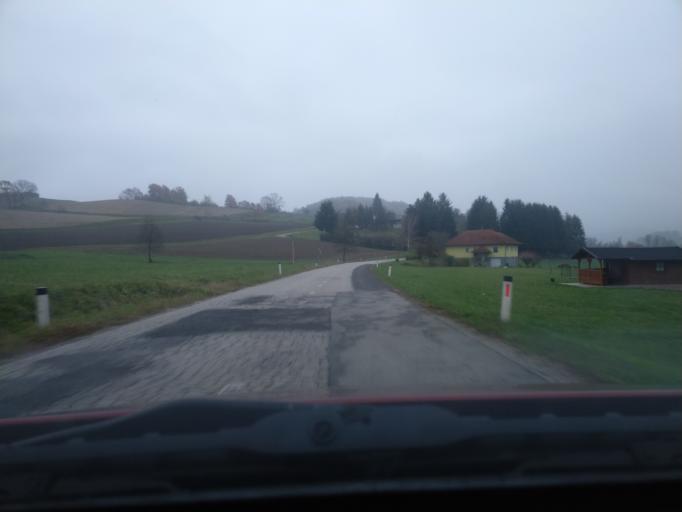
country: SI
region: Kungota
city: Zgornja Kungota
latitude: 46.6608
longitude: 15.6114
